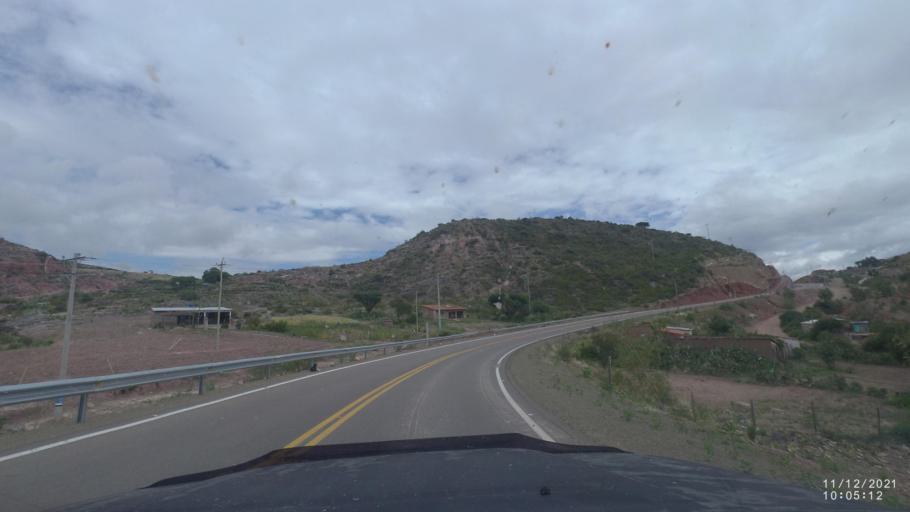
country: BO
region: Cochabamba
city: Cliza
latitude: -17.7022
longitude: -65.9478
